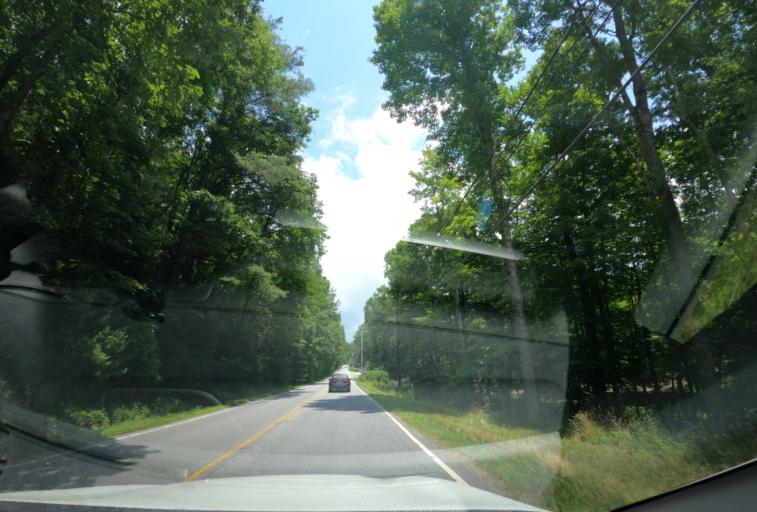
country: US
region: North Carolina
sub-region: Jackson County
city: Cullowhee
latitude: 35.1084
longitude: -83.1189
